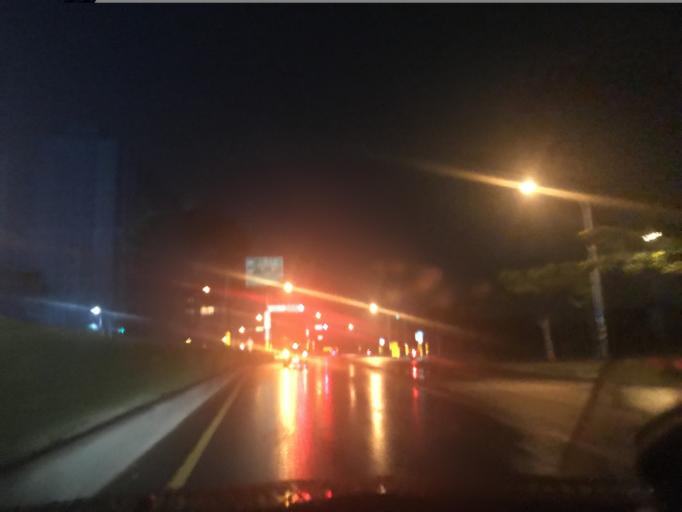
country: TW
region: Taiwan
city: Daxi
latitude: 24.9258
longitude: 121.2810
